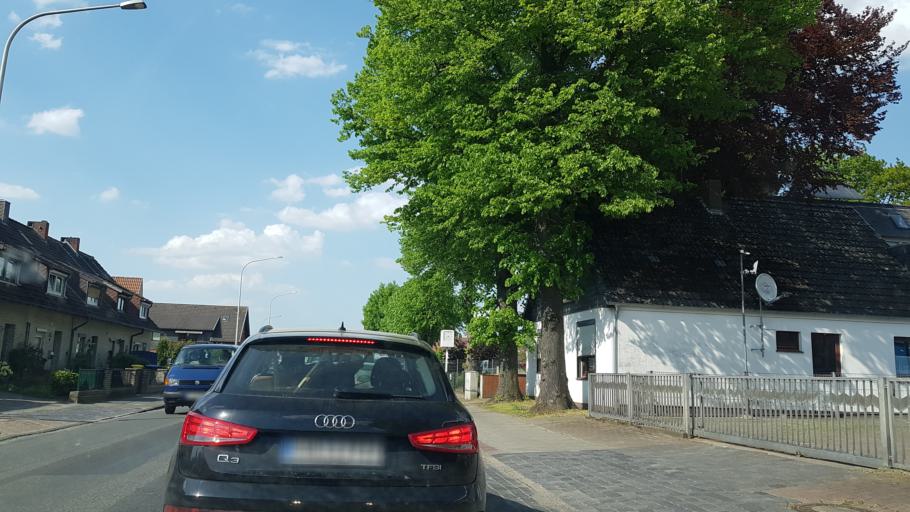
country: DE
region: Lower Saxony
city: Langen
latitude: 53.6055
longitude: 8.5949
